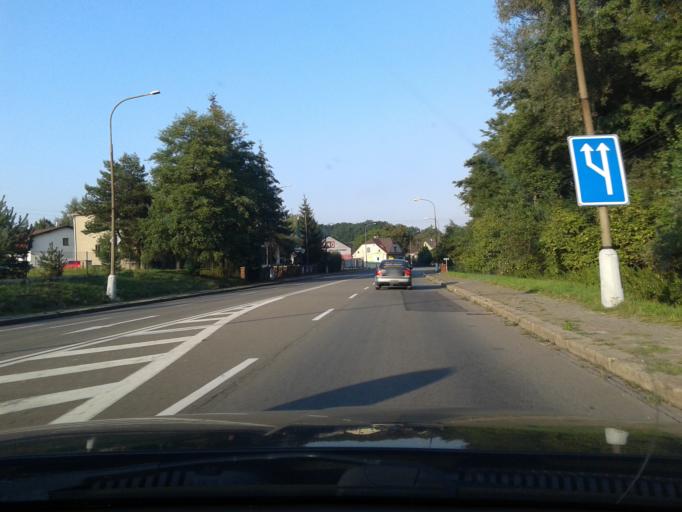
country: CZ
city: Petrvald
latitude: 49.8288
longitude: 18.3769
